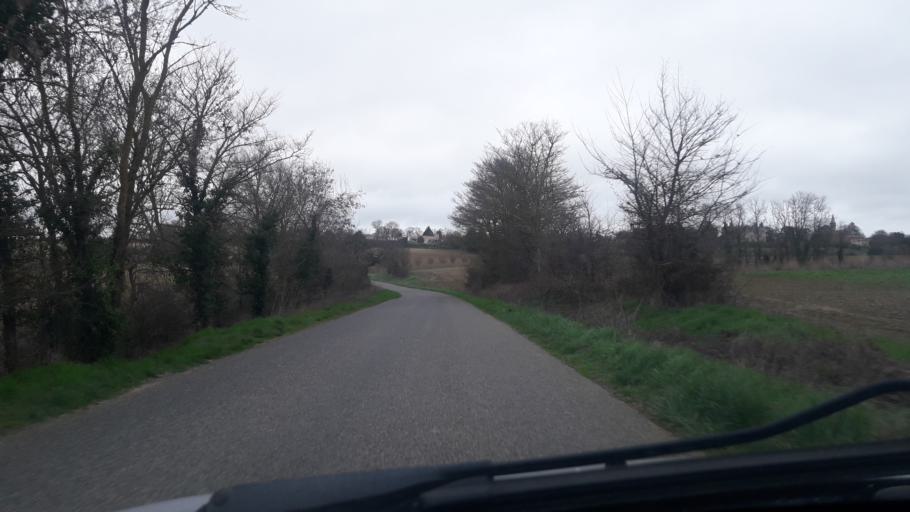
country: FR
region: Midi-Pyrenees
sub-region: Departement du Gers
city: Gimont
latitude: 43.6598
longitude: 1.0132
